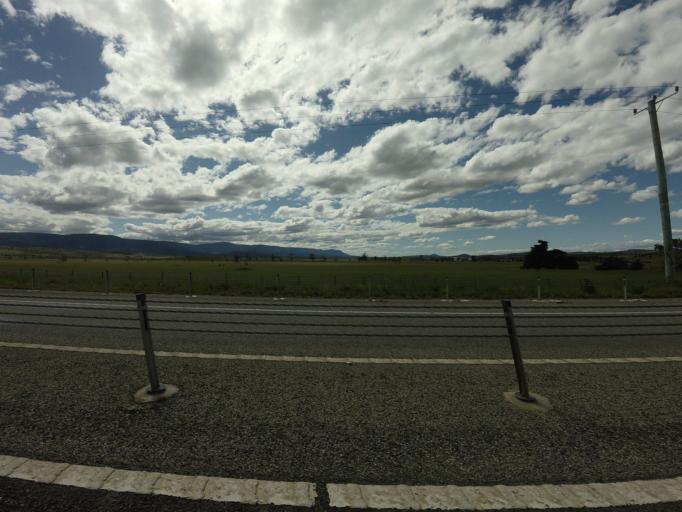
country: AU
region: Tasmania
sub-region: Northern Midlands
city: Evandale
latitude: -42.1528
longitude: 147.4064
